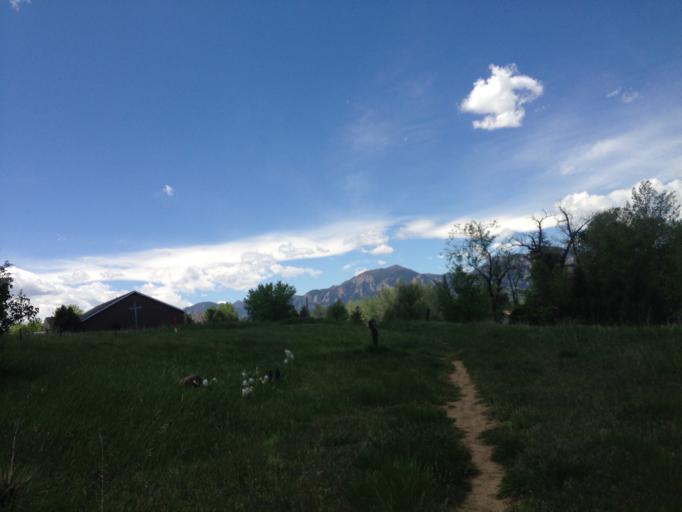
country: US
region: Colorado
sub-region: Boulder County
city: Gunbarrel
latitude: 40.0151
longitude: -105.1942
